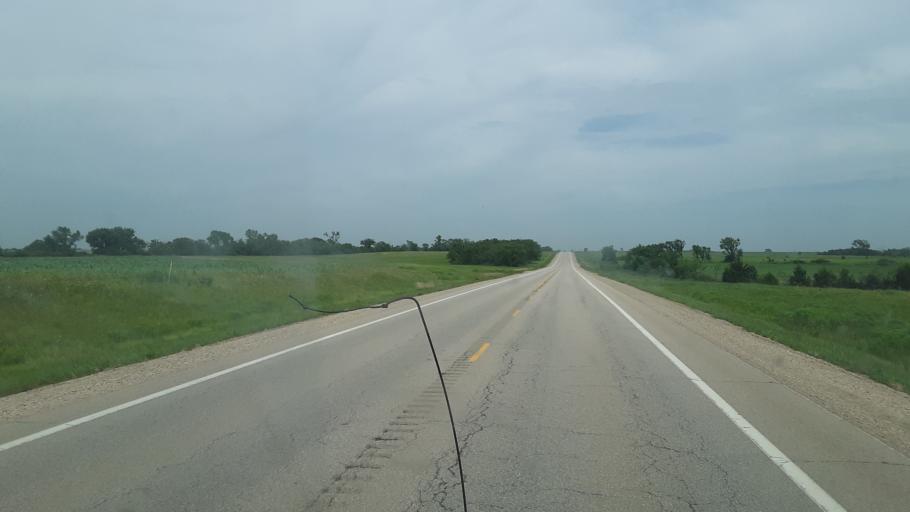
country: US
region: Kansas
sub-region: Woodson County
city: Yates Center
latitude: 37.8559
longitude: -95.8222
